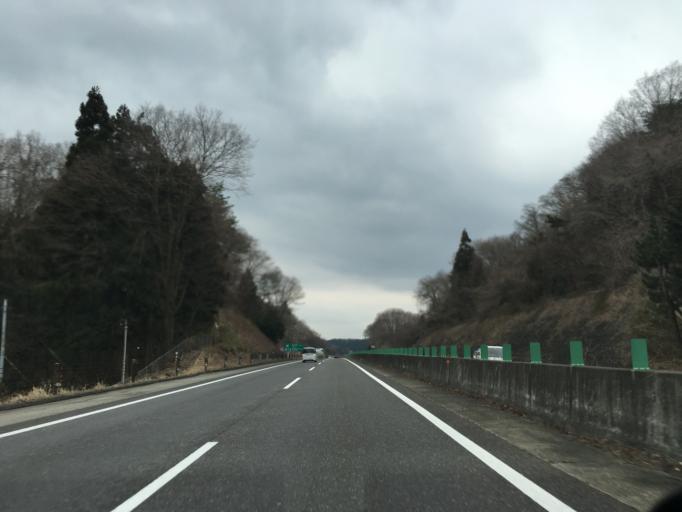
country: JP
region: Fukushima
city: Sukagawa
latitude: 37.1700
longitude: 140.2706
